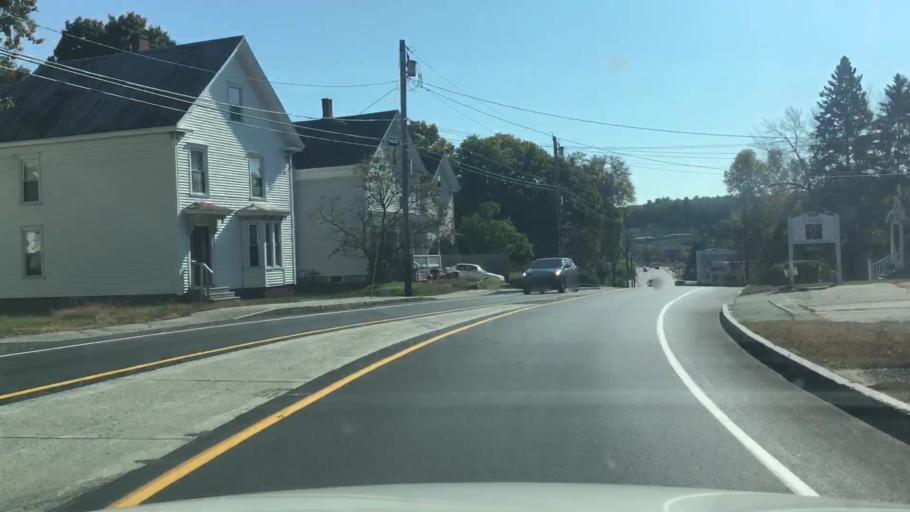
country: US
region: Maine
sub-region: Androscoggin County
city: Lisbon Falls
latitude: 44.0005
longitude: -70.0625
